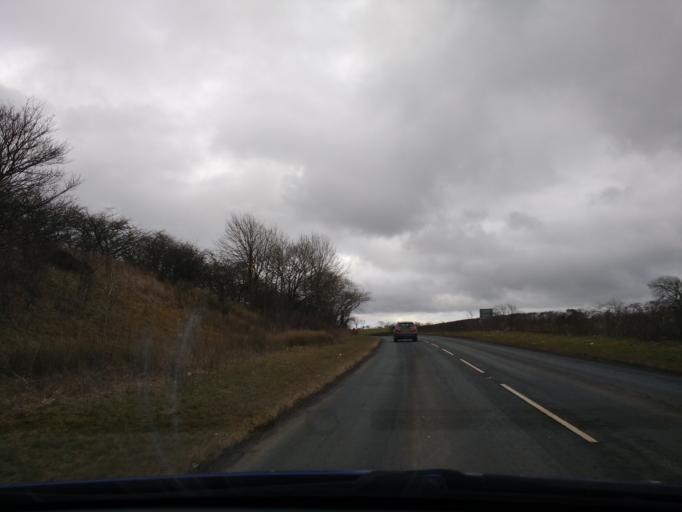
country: GB
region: England
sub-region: Cumbria
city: Dearham
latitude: 54.6926
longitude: -3.4104
